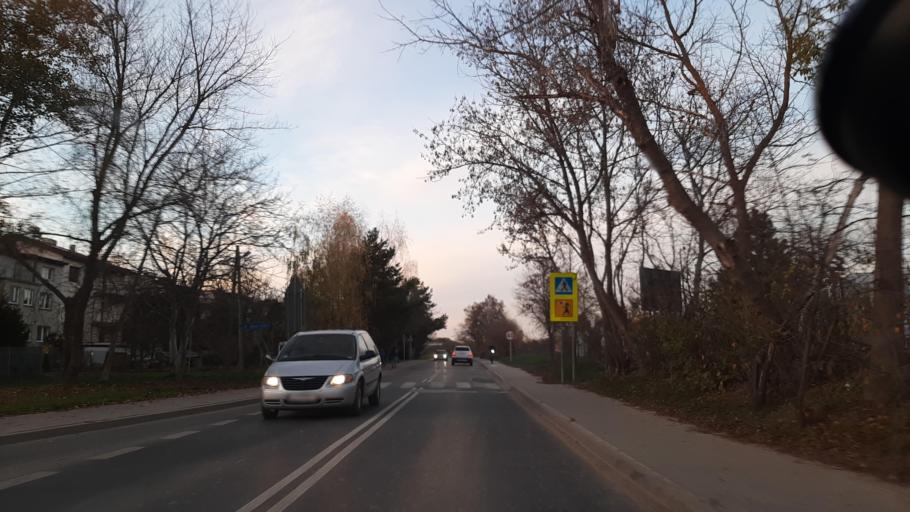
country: PL
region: Lublin Voivodeship
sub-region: Powiat lubelski
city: Lublin
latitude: 51.2718
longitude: 22.5107
